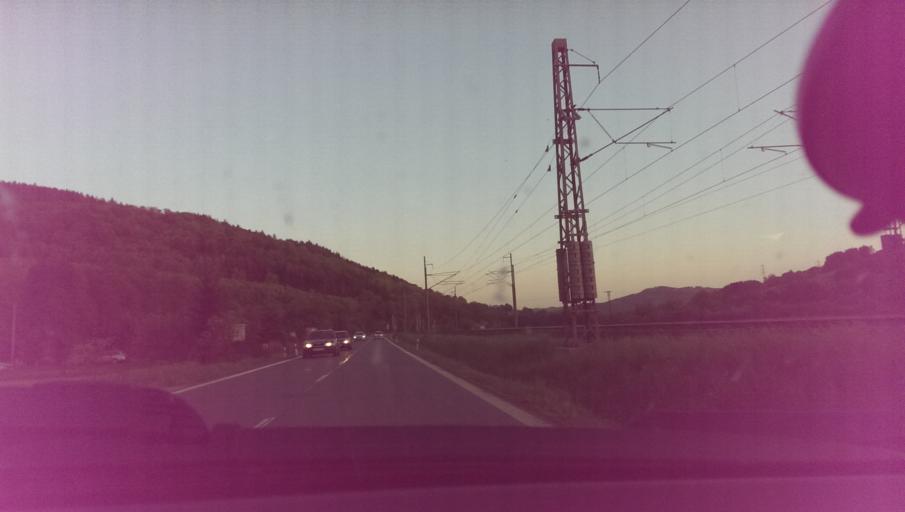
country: CZ
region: Zlin
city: Jablunka
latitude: 49.4104
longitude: 17.9531
